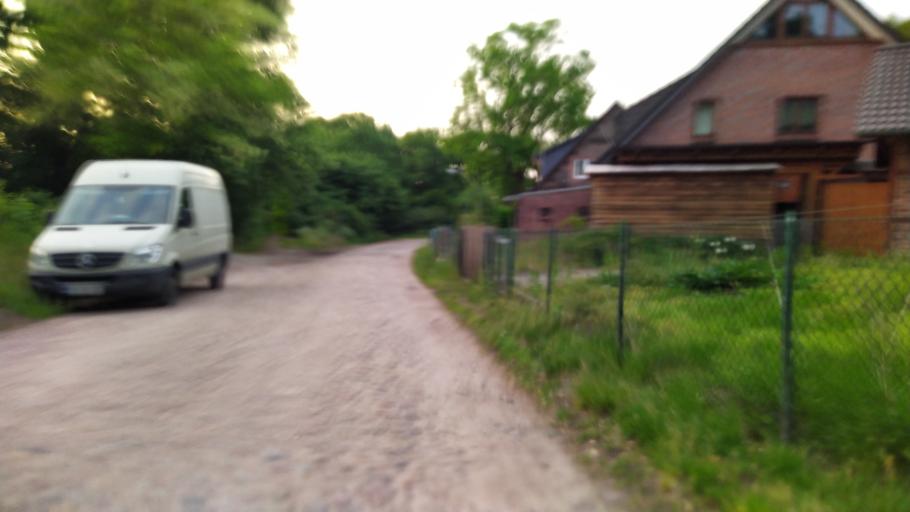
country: DE
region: Lower Saxony
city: Neu Wulmstorf
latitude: 53.4737
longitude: 9.8288
